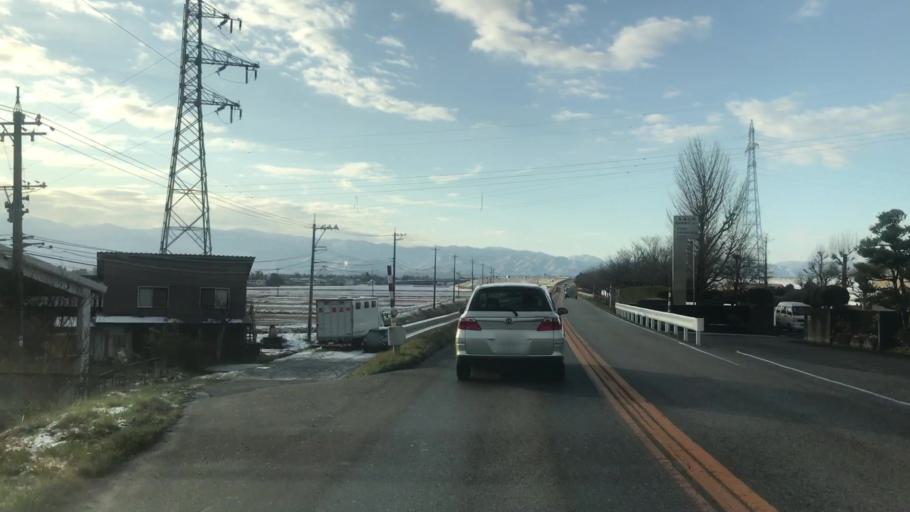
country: JP
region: Toyama
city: Toyama-shi
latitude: 36.6846
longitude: 137.2845
